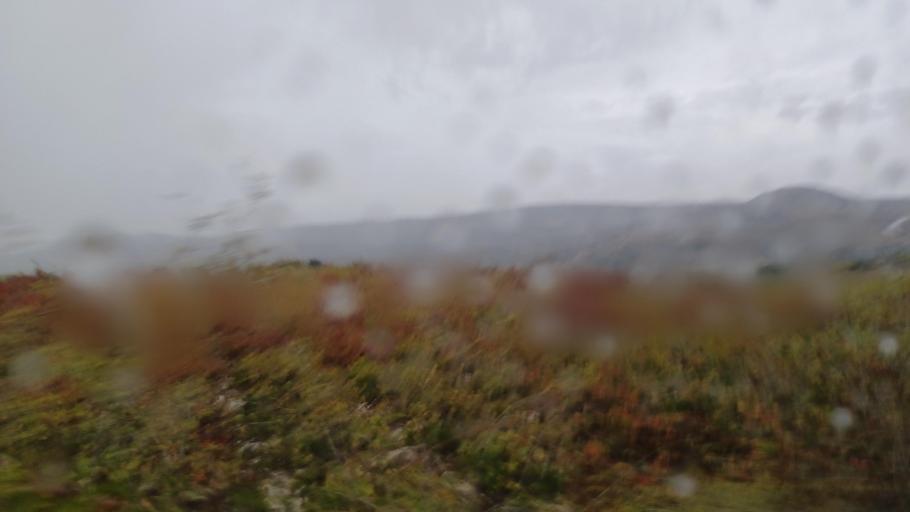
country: CY
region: Pafos
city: Tala
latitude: 34.8936
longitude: 32.4631
